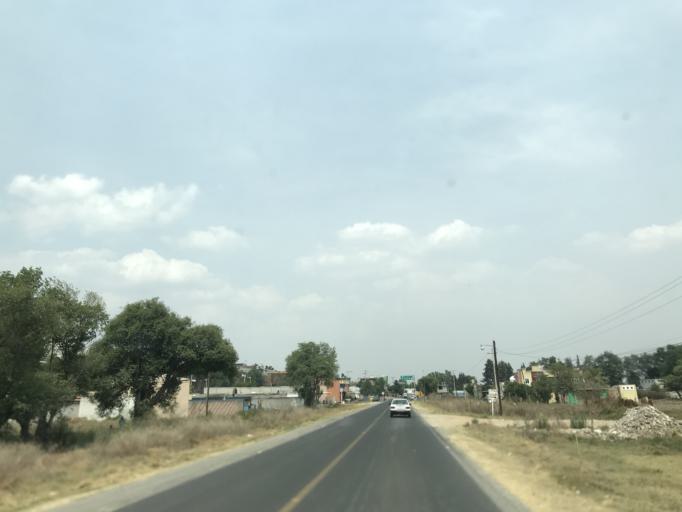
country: MX
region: Tlaxcala
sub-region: Ixtacuixtla de Mariano Matamoros
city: Santa Justina Ecatepec
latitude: 19.3086
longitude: -98.3572
